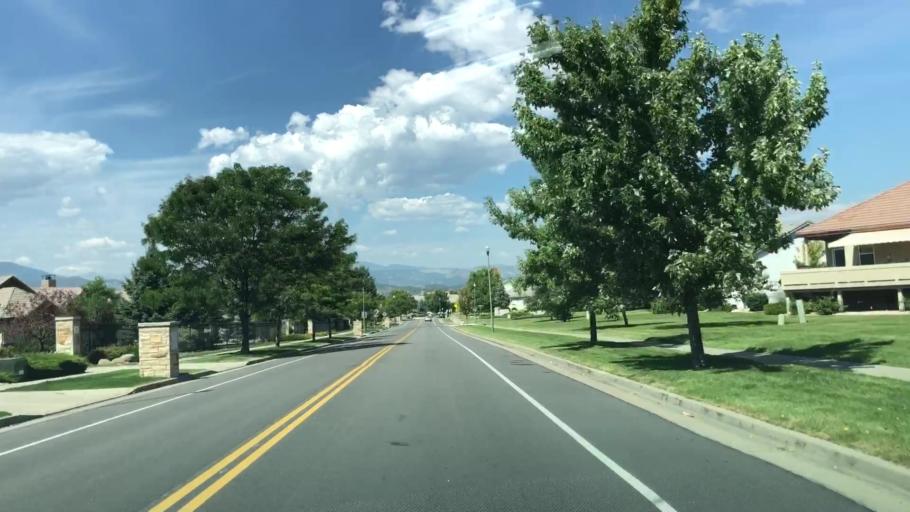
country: US
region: Colorado
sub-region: Larimer County
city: Loveland
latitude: 40.3954
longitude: -105.1419
